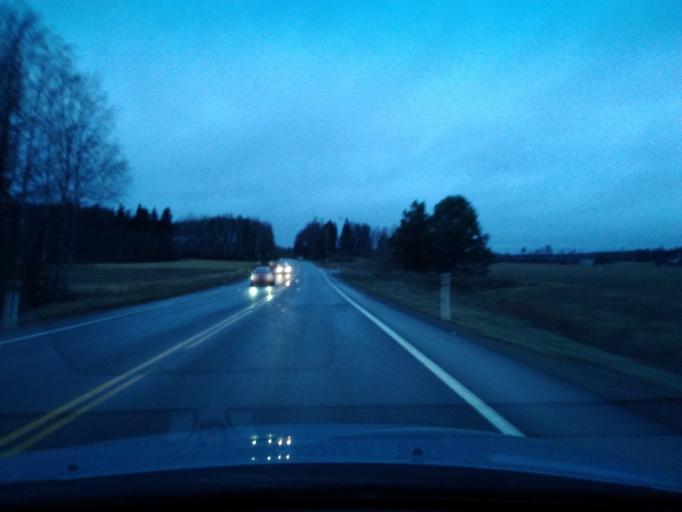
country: FI
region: Uusimaa
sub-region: Porvoo
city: Porvoo
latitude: 60.4028
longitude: 25.5928
